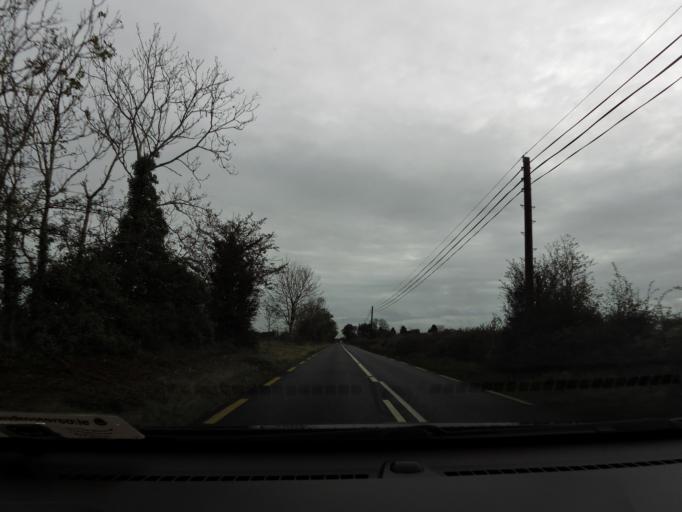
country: IE
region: Connaught
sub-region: County Galway
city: Tuam
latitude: 53.5998
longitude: -8.7633
